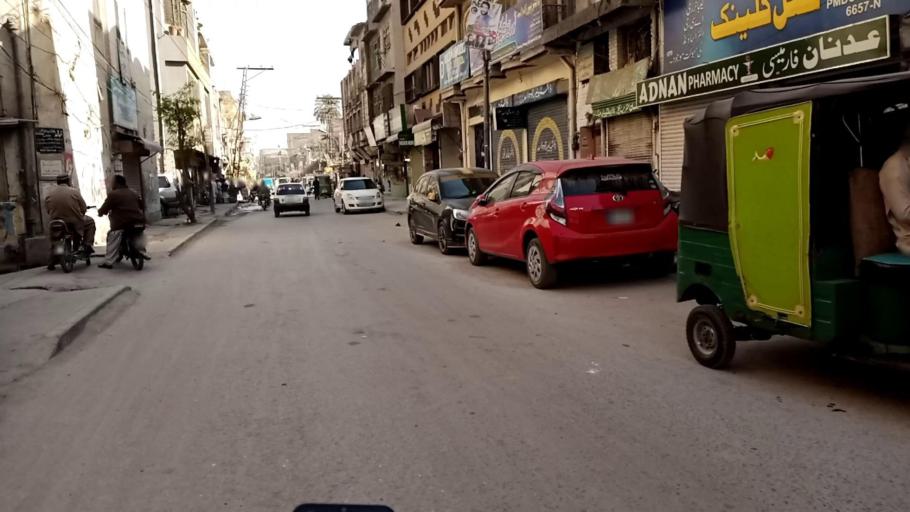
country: PK
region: Khyber Pakhtunkhwa
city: Peshawar
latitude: 34.0070
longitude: 71.5835
